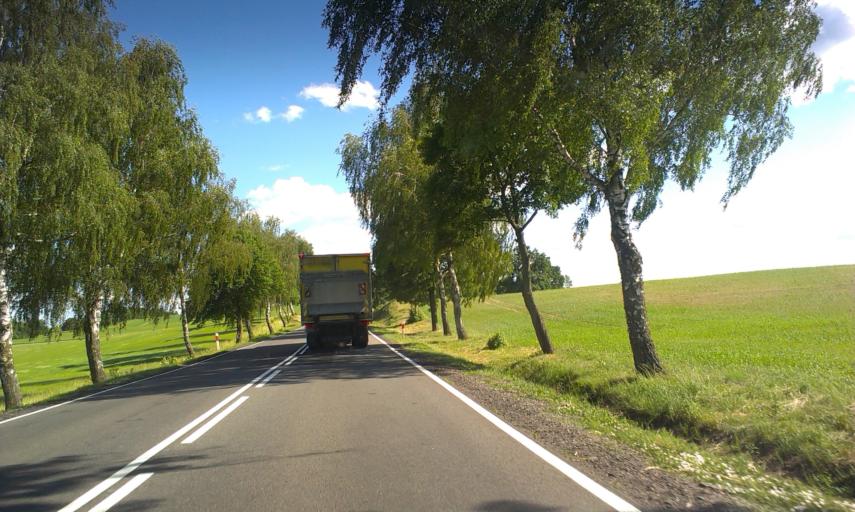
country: PL
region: West Pomeranian Voivodeship
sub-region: Powiat szczecinecki
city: Szczecinek
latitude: 53.7558
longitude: 16.6514
